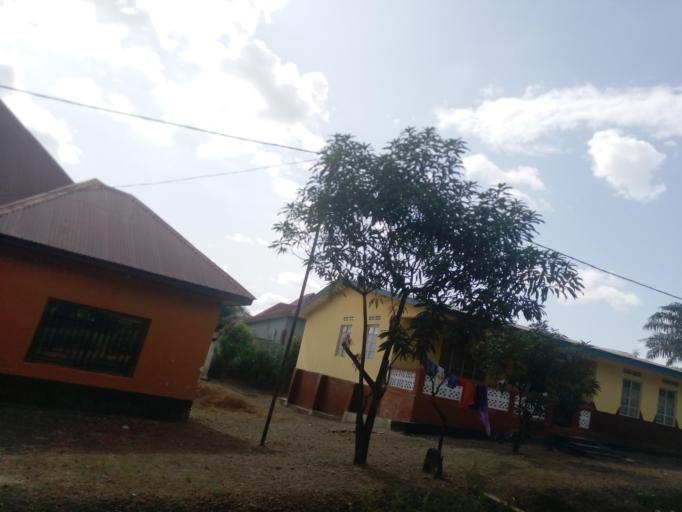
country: SL
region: Northern Province
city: Makeni
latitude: 8.8996
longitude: -12.0320
